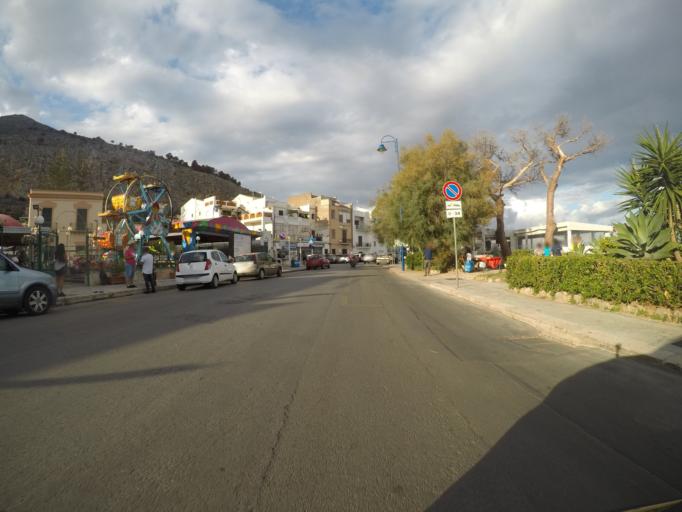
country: IT
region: Sicily
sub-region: Palermo
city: Palermo
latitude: 38.2062
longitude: 13.3252
